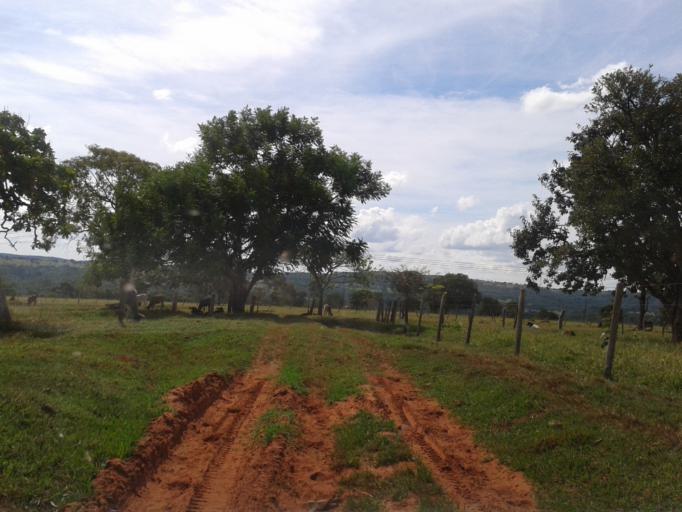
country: BR
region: Minas Gerais
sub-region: Campina Verde
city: Campina Verde
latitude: -19.4365
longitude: -49.6304
